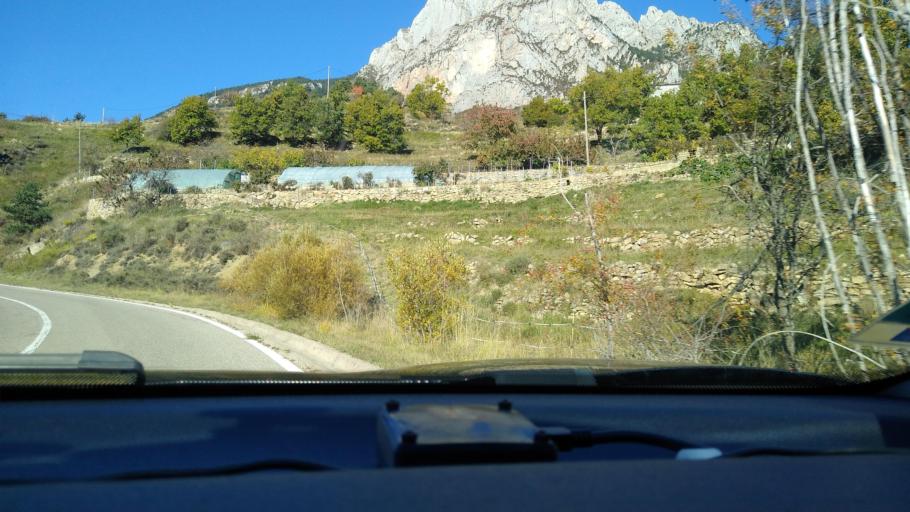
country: ES
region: Catalonia
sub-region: Provincia de Barcelona
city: Saldes
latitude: 42.2236
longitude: 1.7279
